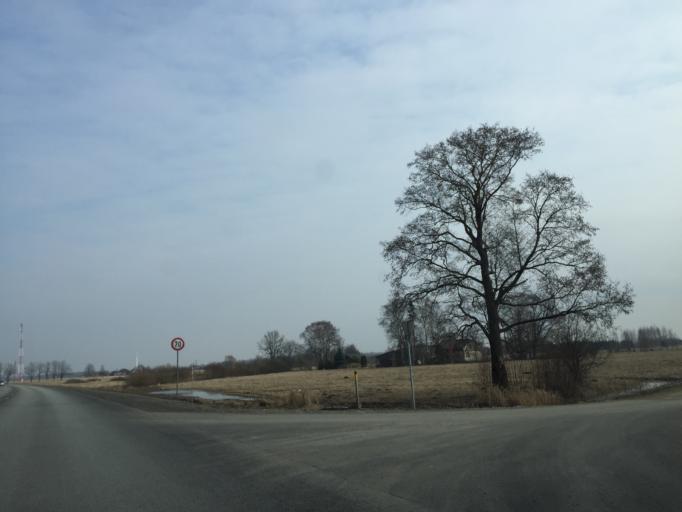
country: LV
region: Salacgrivas
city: Ainazi
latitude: 57.8548
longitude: 24.3627
